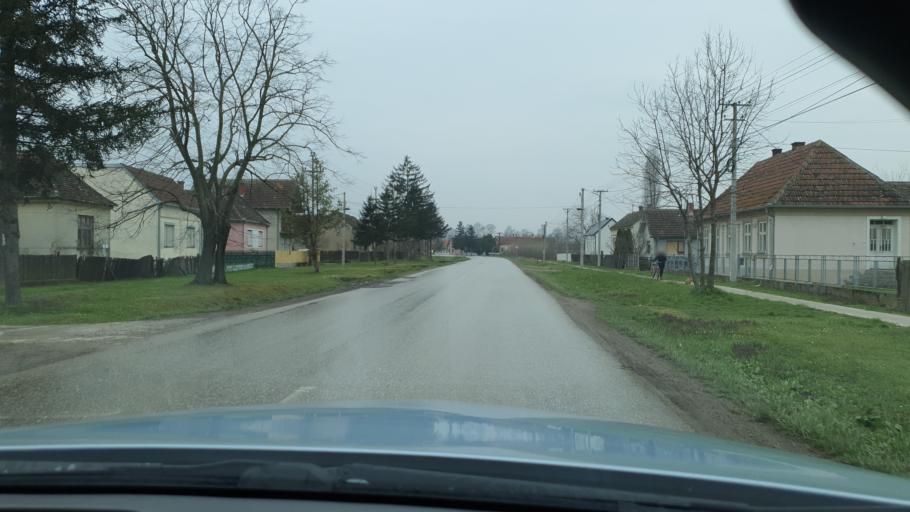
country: RS
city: Stitar
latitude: 44.7911
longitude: 19.5882
